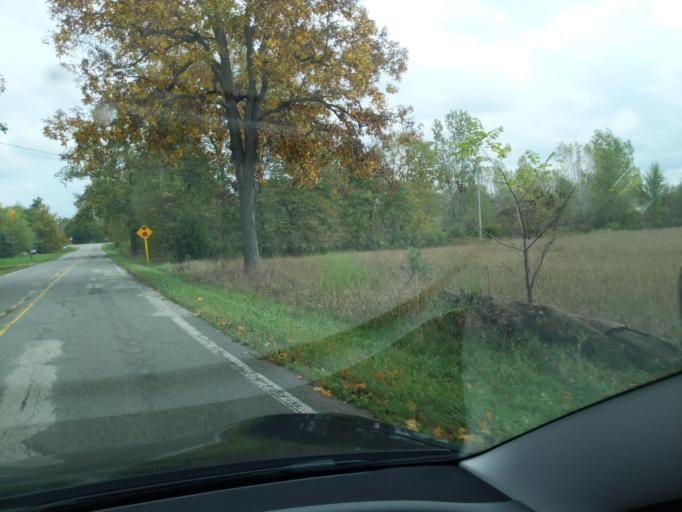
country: US
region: Michigan
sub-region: Ingham County
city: Leslie
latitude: 42.4127
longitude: -84.3556
